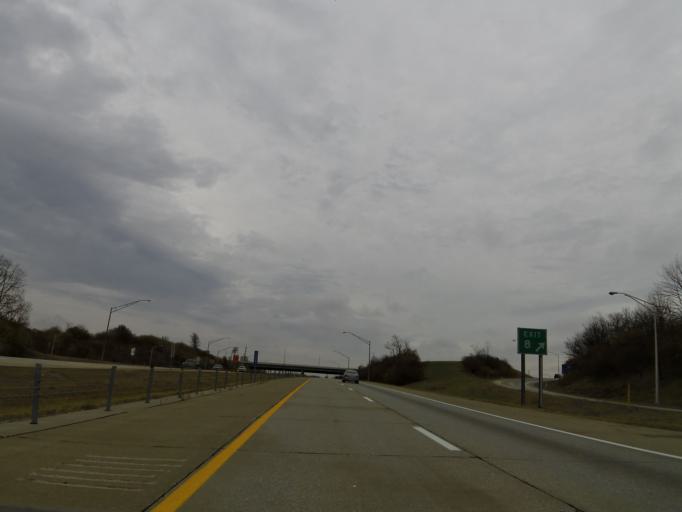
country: US
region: Kentucky
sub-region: Boone County
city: Hebron
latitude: 39.0806
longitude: -84.7131
